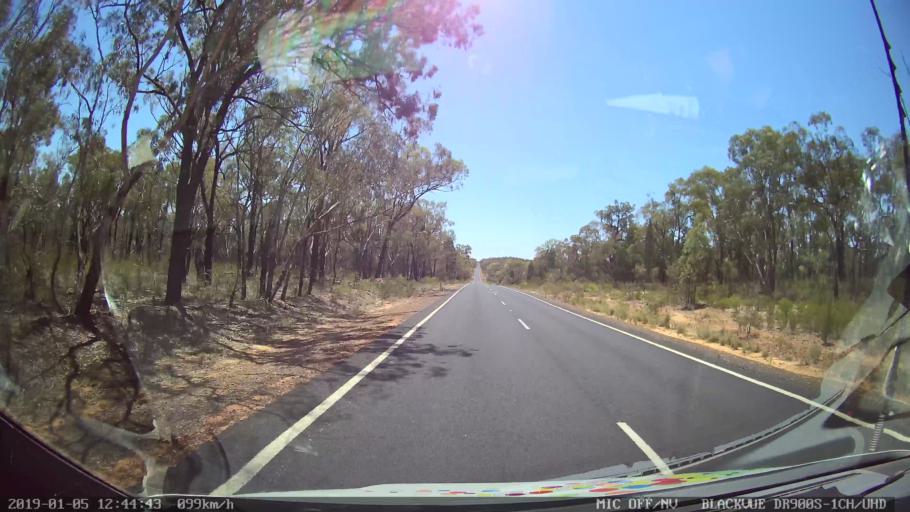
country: AU
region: New South Wales
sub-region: Warrumbungle Shire
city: Coonabarabran
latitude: -31.1350
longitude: 149.5407
